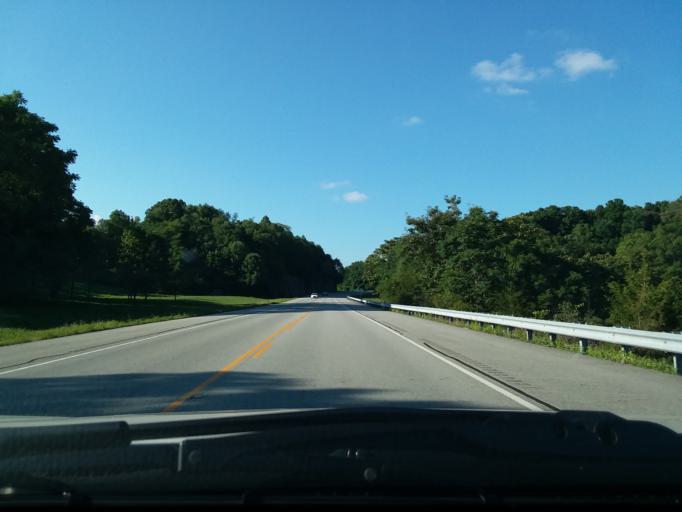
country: US
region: Tennessee
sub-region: Clay County
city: Celina
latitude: 36.5737
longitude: -85.4478
